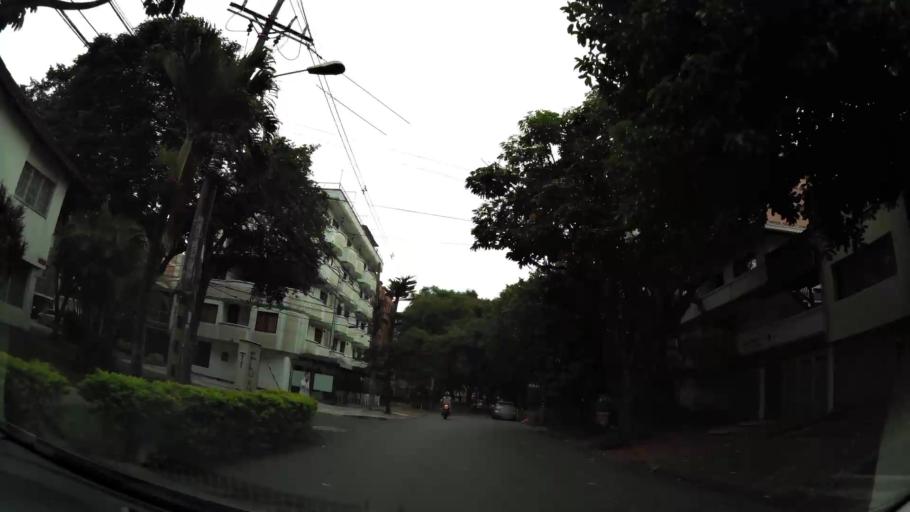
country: CO
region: Antioquia
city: Medellin
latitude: 6.2567
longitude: -75.5848
